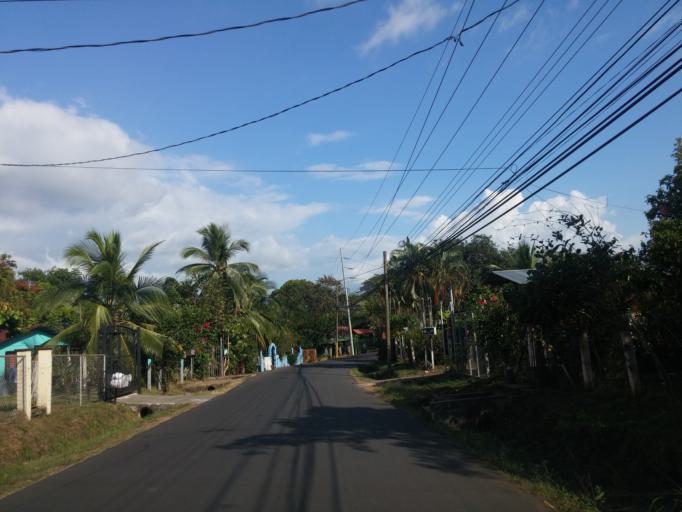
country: CR
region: Alajuela
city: Orotina
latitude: 9.9174
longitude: -84.5441
